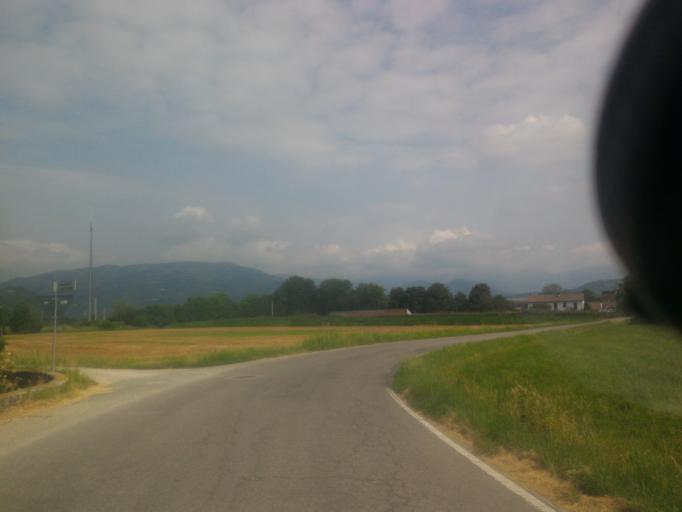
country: IT
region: Piedmont
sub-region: Provincia di Torino
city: San Secondo di Pinerolo
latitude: 44.8601
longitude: 7.3200
